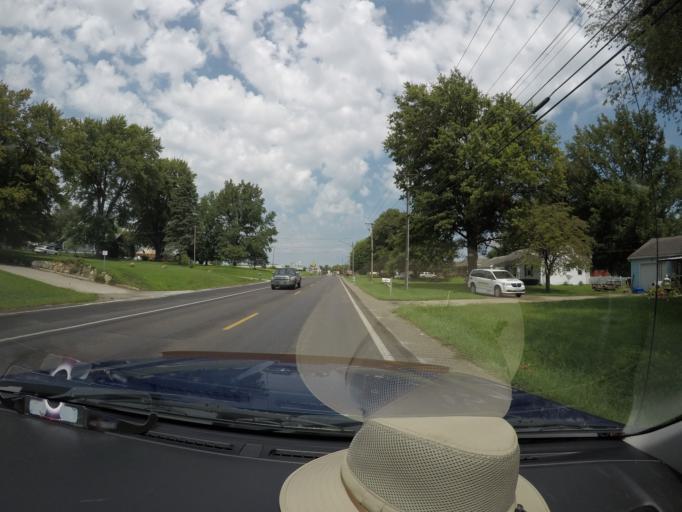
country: US
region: Missouri
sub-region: Lafayette County
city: Lexington
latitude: 39.1648
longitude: -93.8798
